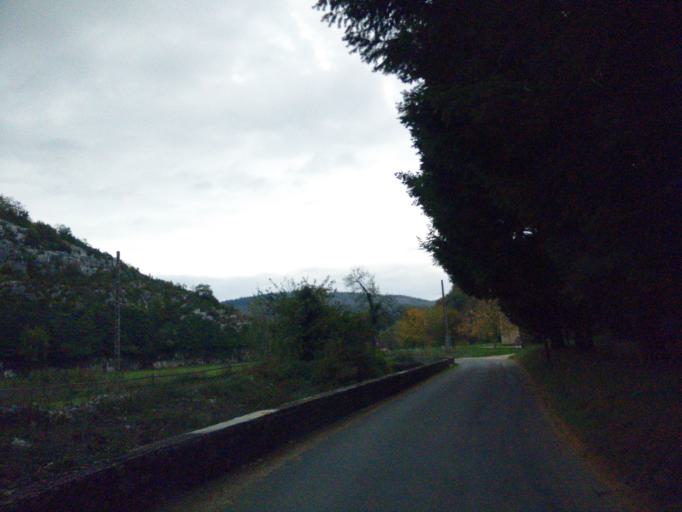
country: FR
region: Midi-Pyrenees
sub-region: Departement du Lot
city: Cajarc
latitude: 44.5095
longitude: 1.6495
